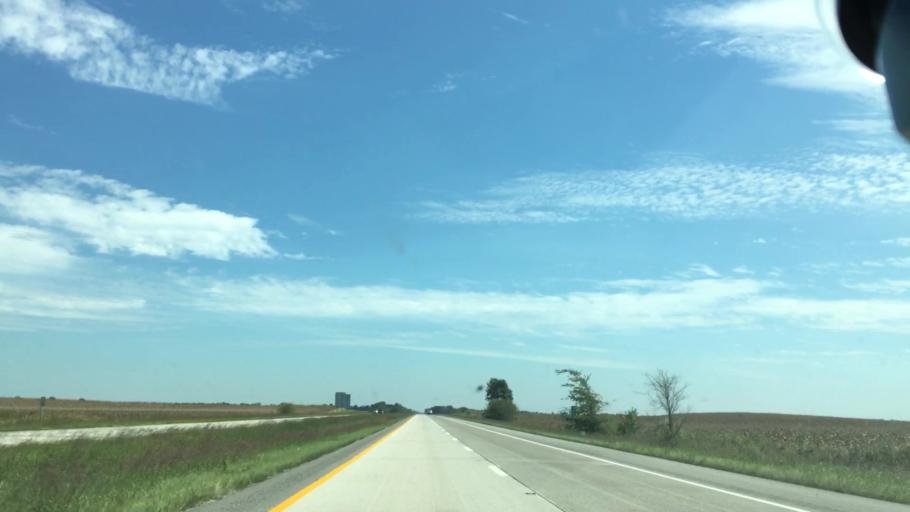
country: US
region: Kentucky
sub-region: Henderson County
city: Henderson
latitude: 37.8053
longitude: -87.5295
